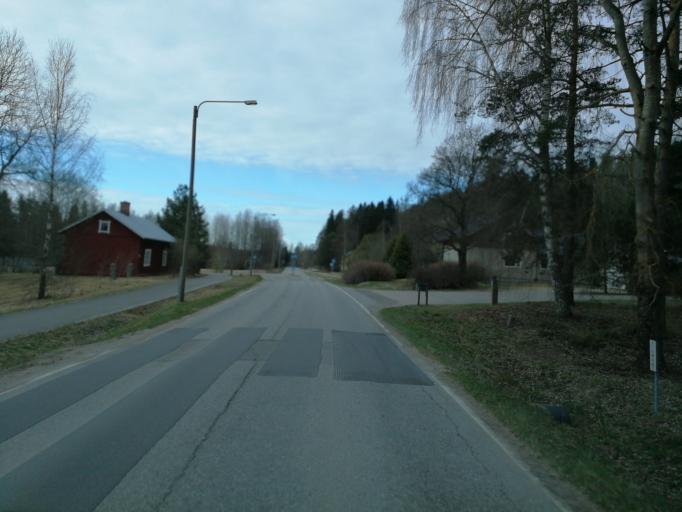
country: FI
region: Varsinais-Suomi
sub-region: Salo
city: Muurla
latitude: 60.3654
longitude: 23.2984
